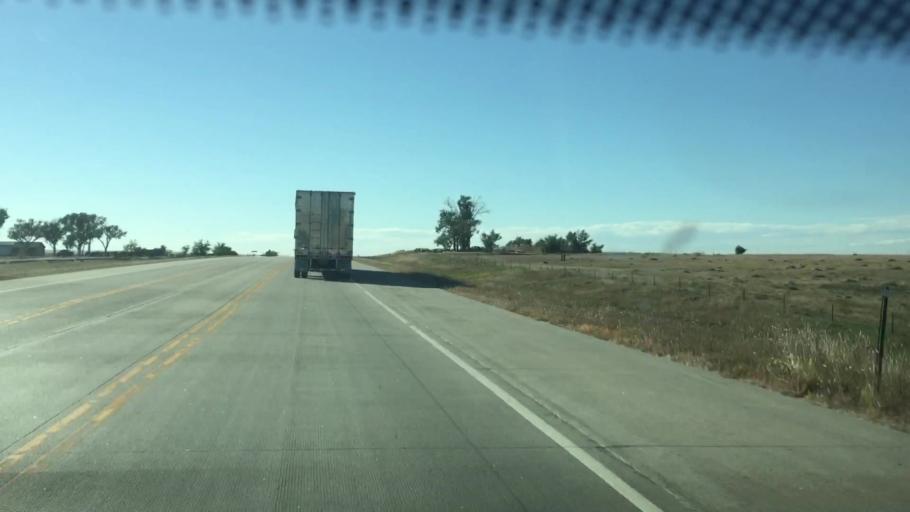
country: US
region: Colorado
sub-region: Kiowa County
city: Eads
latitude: 38.8260
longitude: -103.0072
